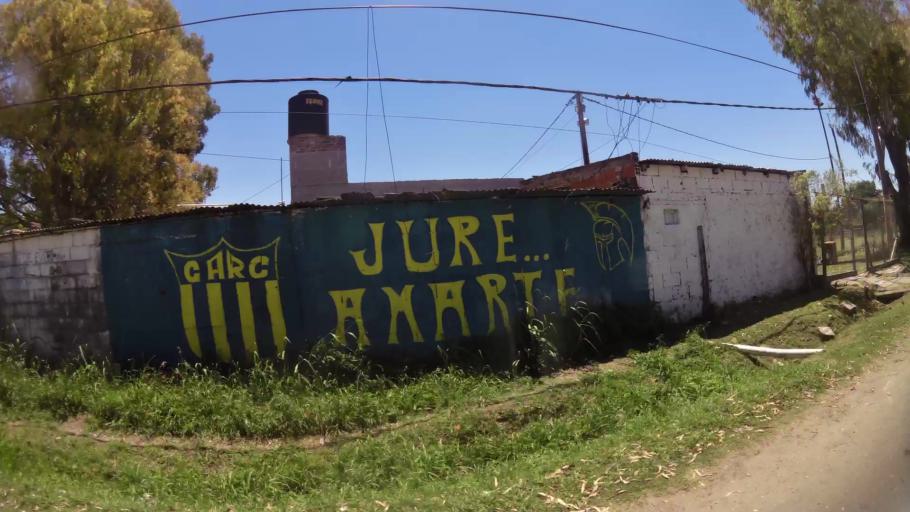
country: AR
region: Santa Fe
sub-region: Departamento de Rosario
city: Rosario
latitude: -32.9543
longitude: -60.7051
